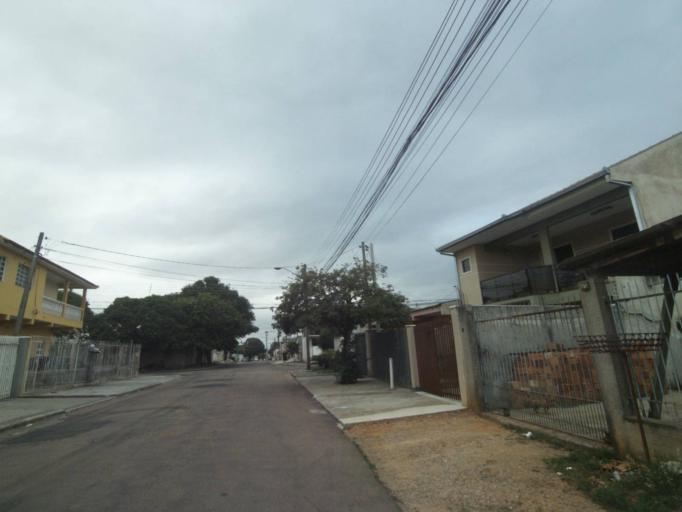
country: BR
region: Parana
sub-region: Sao Jose Dos Pinhais
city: Sao Jose dos Pinhais
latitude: -25.5488
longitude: -49.2576
